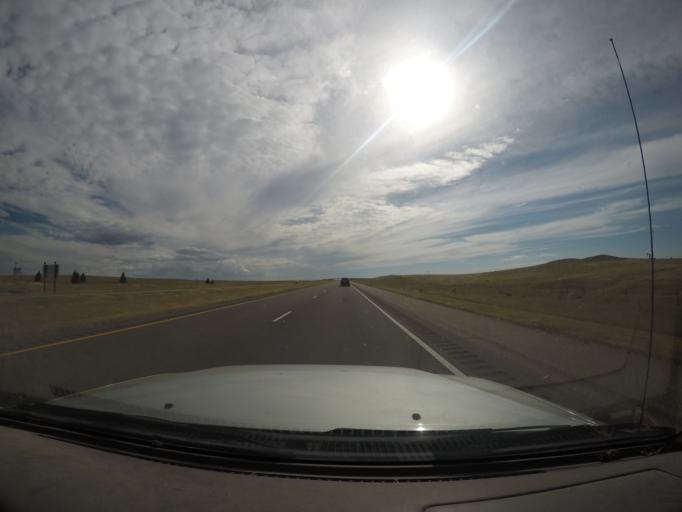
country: US
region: Nebraska
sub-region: Kimball County
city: Kimball
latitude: 41.2099
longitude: -103.7041
